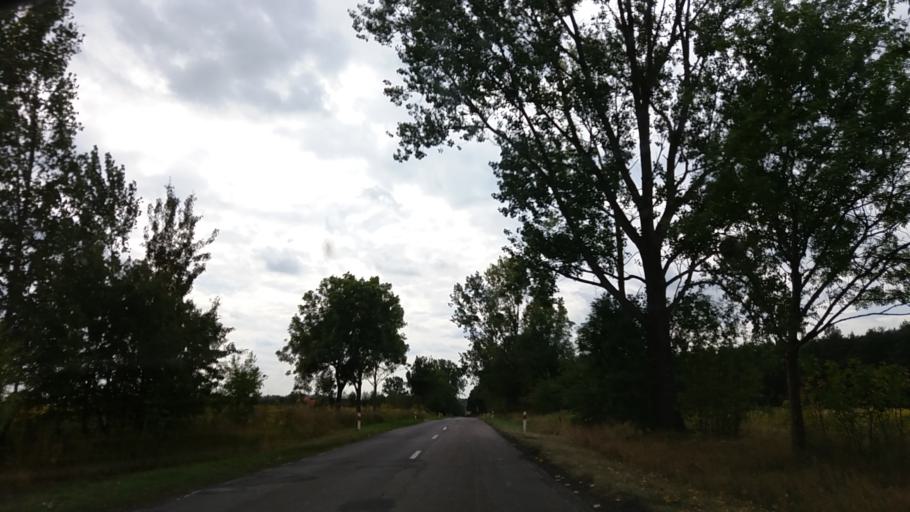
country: PL
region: West Pomeranian Voivodeship
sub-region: Powiat stargardzki
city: Kobylanka
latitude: 53.3322
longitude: 14.8582
